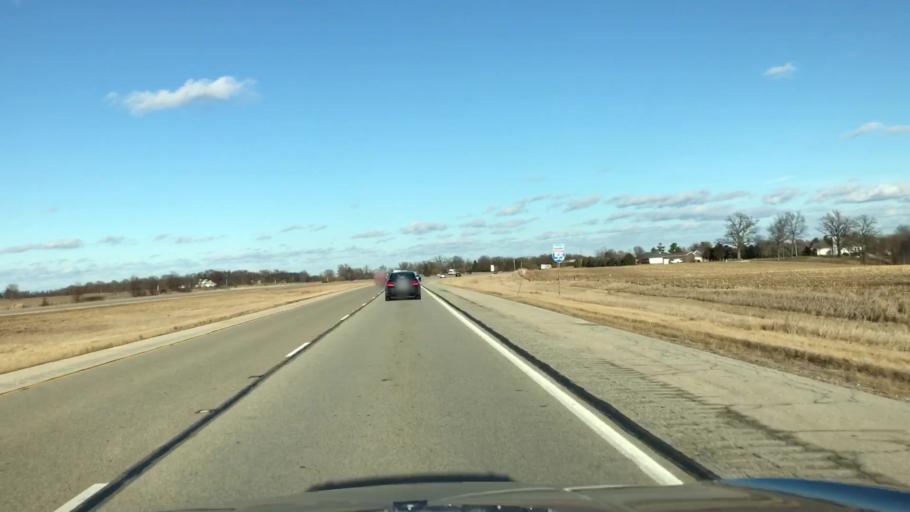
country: US
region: Illinois
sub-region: McLean County
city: Hudson
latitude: 40.5769
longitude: -88.8950
